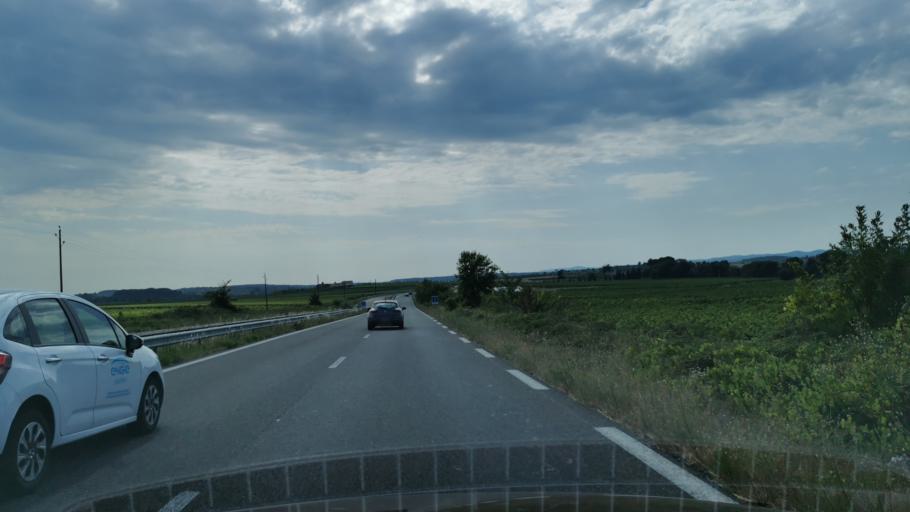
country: FR
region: Languedoc-Roussillon
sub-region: Departement de l'Herault
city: Cazouls-les-Beziers
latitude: 43.3657
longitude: 3.0771
